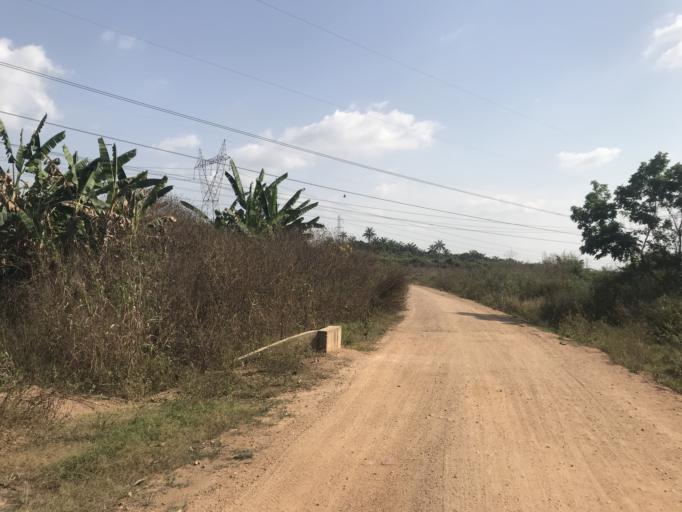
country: NG
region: Osun
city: Ikirun
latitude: 7.8702
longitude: 4.5852
